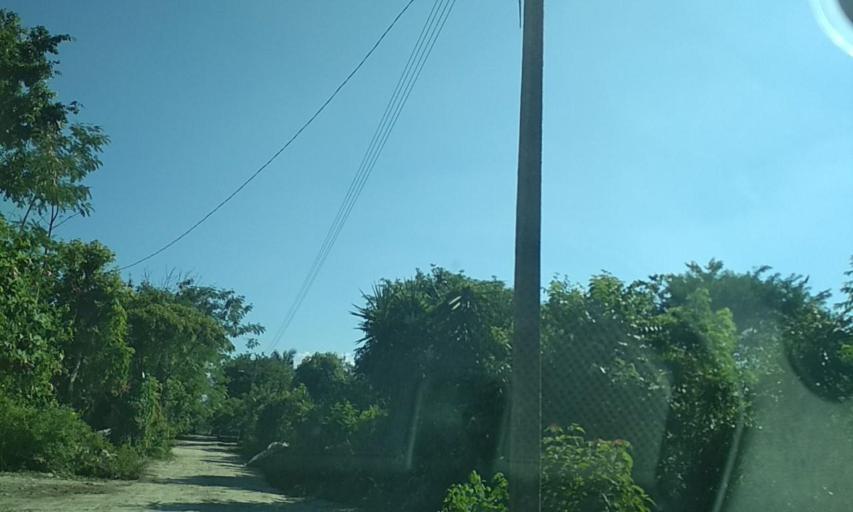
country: MX
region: Veracruz
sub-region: Martinez de la Torre
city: La Union Paso Largo
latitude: 20.1419
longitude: -97.0029
